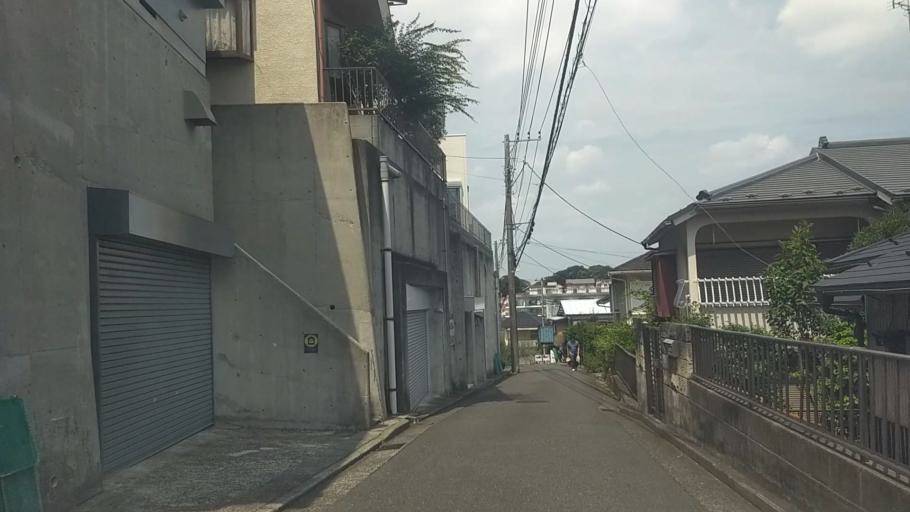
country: JP
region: Kanagawa
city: Yokohama
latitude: 35.5070
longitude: 139.6261
